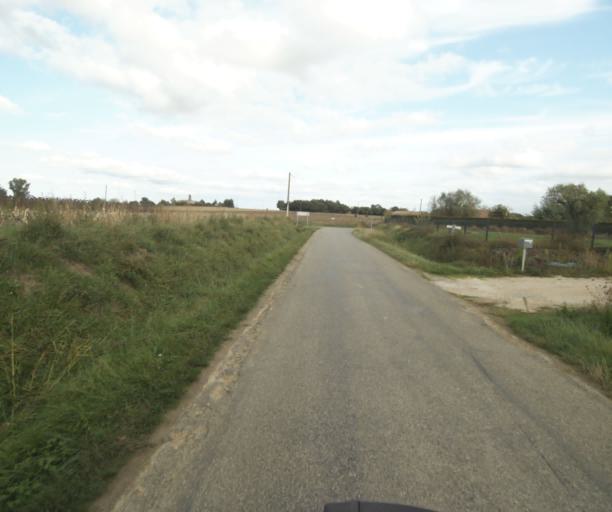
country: FR
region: Midi-Pyrenees
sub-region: Departement du Tarn-et-Garonne
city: Verdun-sur-Garonne
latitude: 43.8416
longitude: 1.1269
